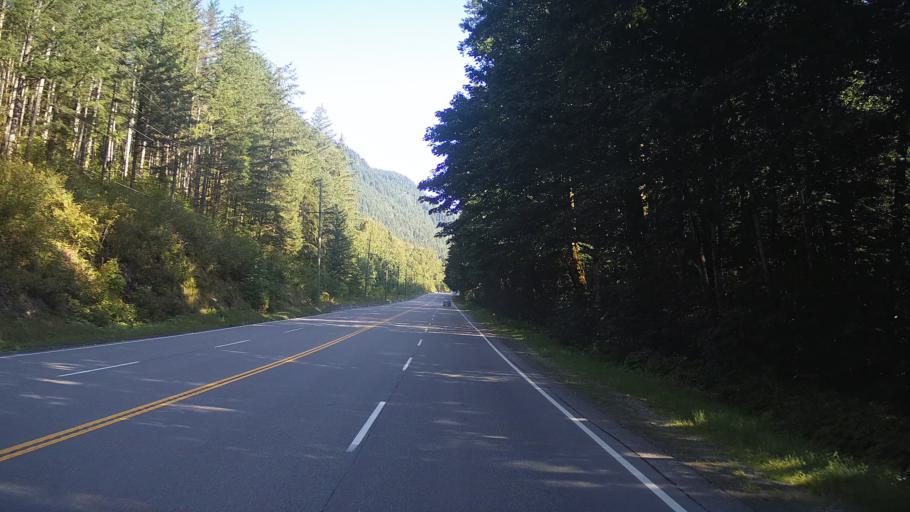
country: CA
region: British Columbia
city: Hope
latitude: 49.4433
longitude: -121.4365
